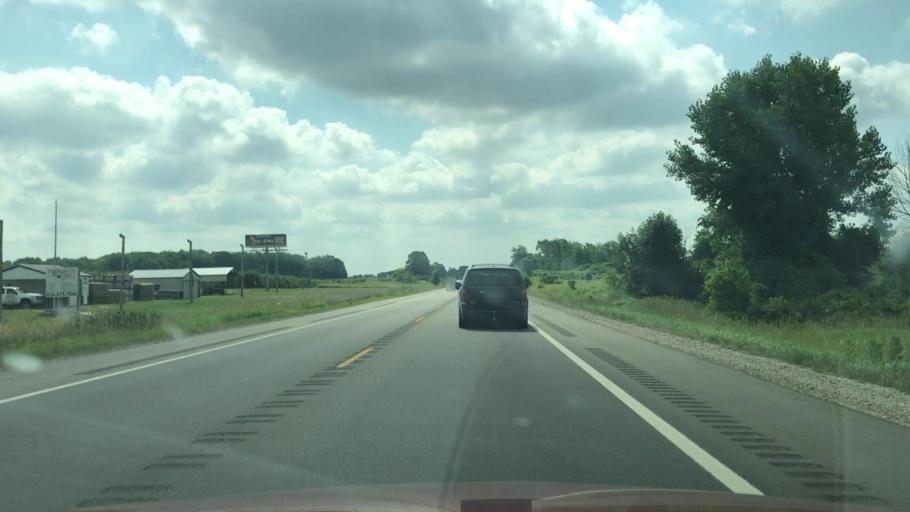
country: US
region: Michigan
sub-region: Kent County
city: Kent City
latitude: 43.2288
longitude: -85.7855
